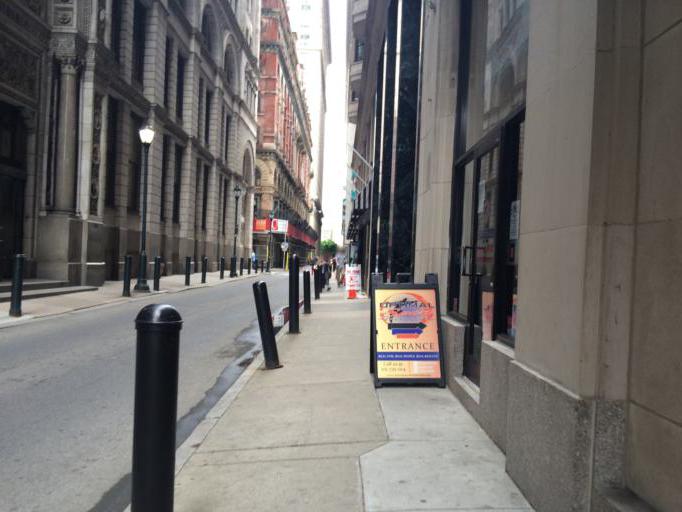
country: US
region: Pennsylvania
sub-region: Philadelphia County
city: Philadelphia
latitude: 39.9494
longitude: -75.1631
